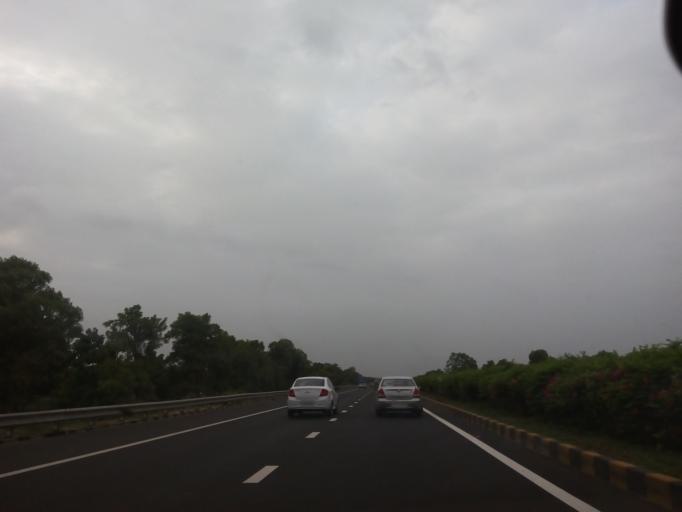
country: IN
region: Gujarat
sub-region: Kheda
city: Chaklasi
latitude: 22.6564
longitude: 72.9250
